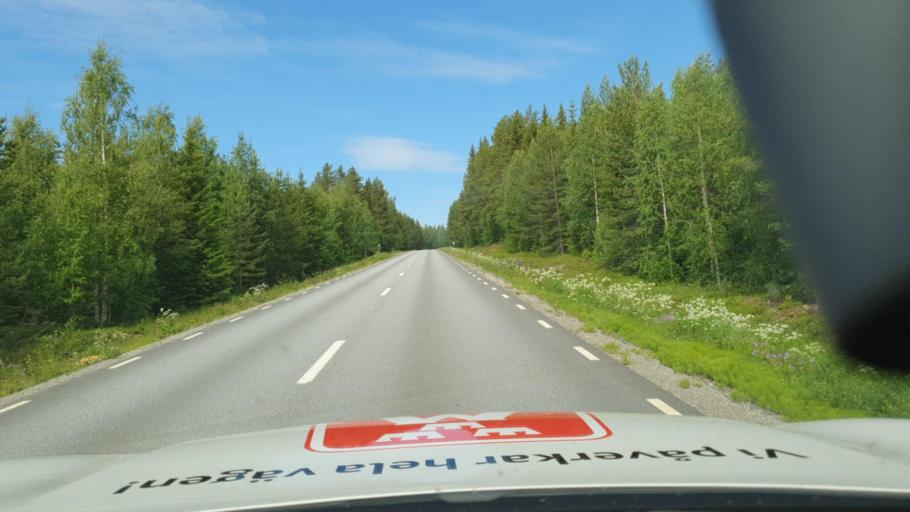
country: SE
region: Vaesterbotten
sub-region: Skelleftea Kommun
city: Forsbacka
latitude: 64.7106
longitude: 20.4274
